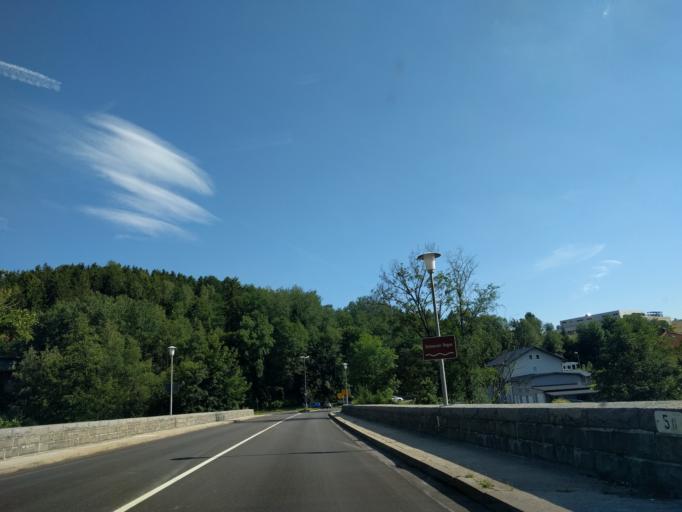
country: DE
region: Bavaria
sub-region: Lower Bavaria
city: Regen
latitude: 48.9737
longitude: 13.1391
